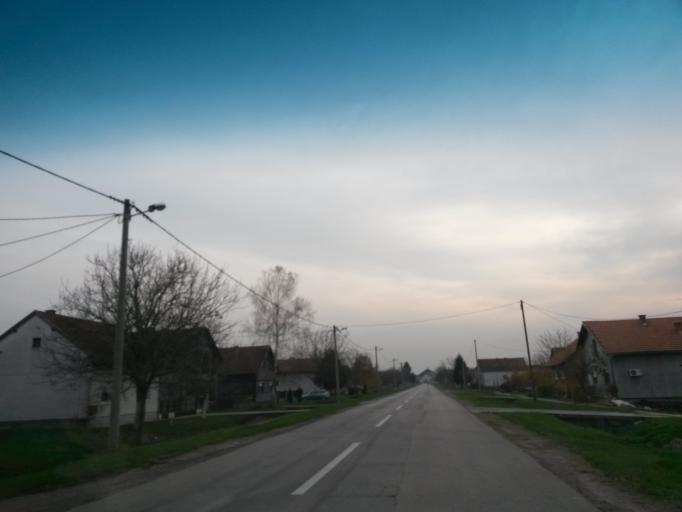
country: HR
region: Vukovarsko-Srijemska
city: Nijemci
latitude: 45.1865
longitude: 19.0150
